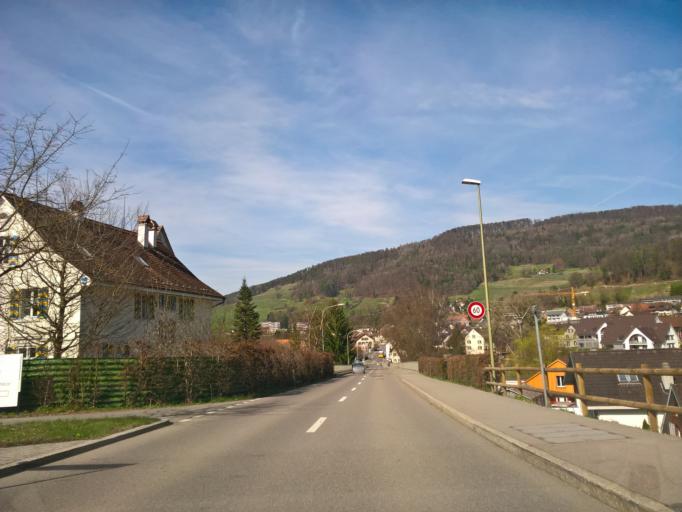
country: CH
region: Zurich
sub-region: Bezirk Buelach
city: Freienstein
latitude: 47.5287
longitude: 8.5810
